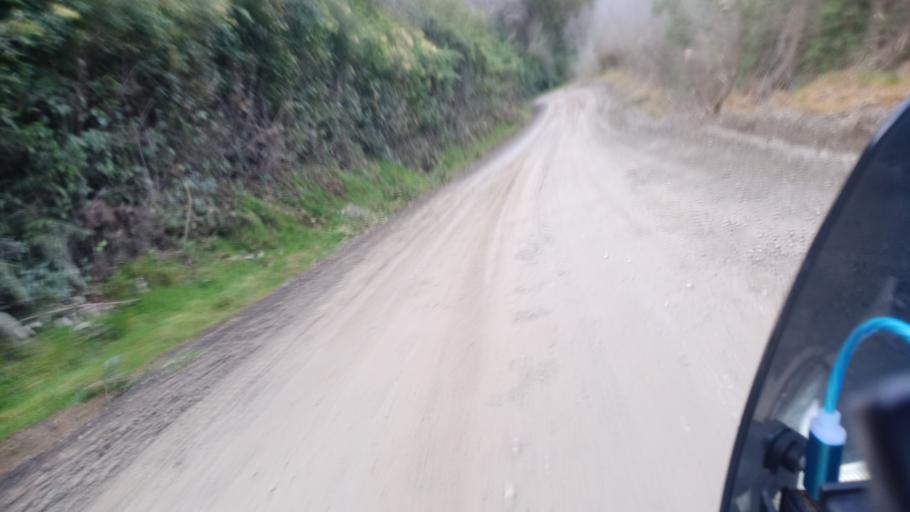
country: NZ
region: Gisborne
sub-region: Gisborne District
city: Gisborne
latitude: -38.1294
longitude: 178.1818
